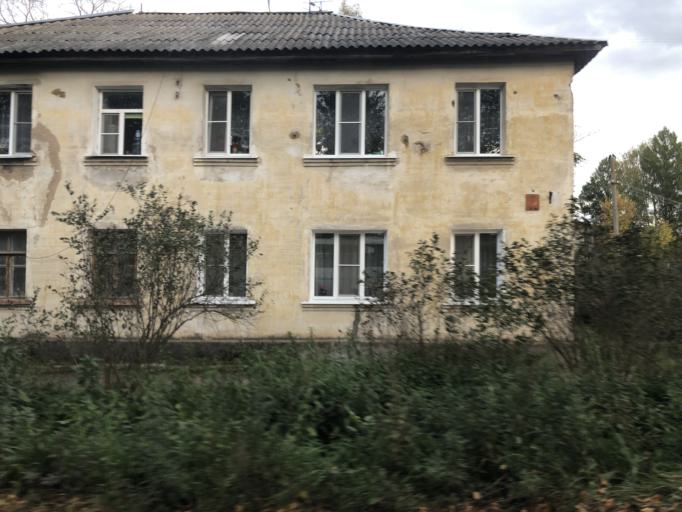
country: RU
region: Tverskaya
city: Rzhev
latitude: 56.2521
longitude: 34.2930
